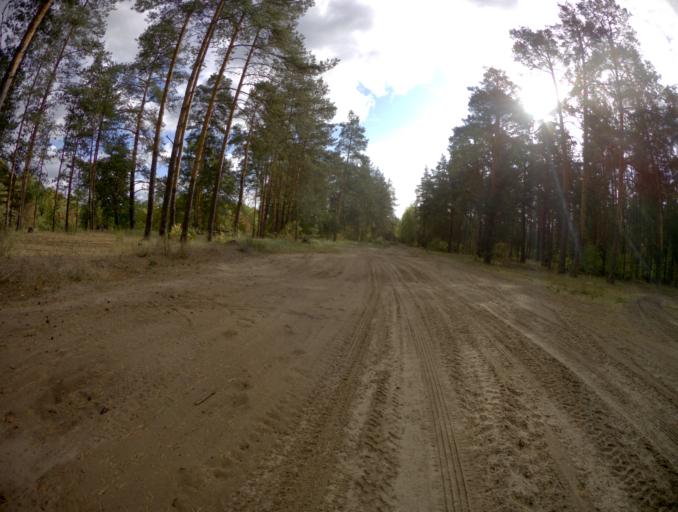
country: RU
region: Vladimir
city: Petushki
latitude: 55.8853
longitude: 39.4995
